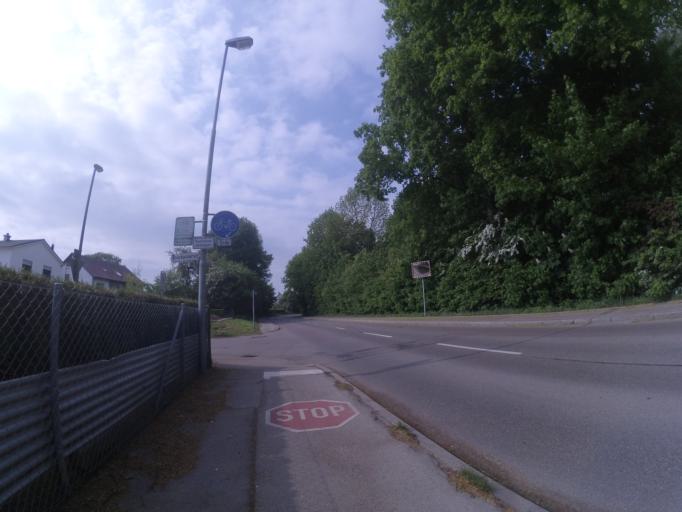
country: DE
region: Baden-Wuerttemberg
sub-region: Tuebingen Region
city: Erbach
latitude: 48.3445
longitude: 9.9425
